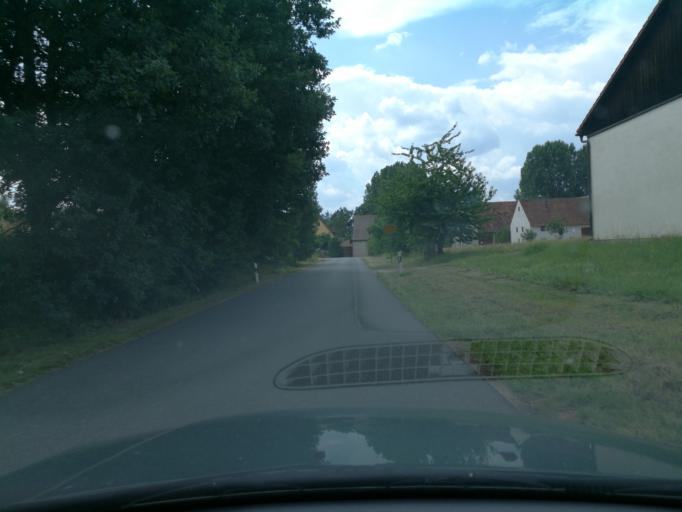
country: DE
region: Bavaria
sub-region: Regierungsbezirk Mittelfranken
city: Grosshabersdorf
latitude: 49.4310
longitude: 10.7845
